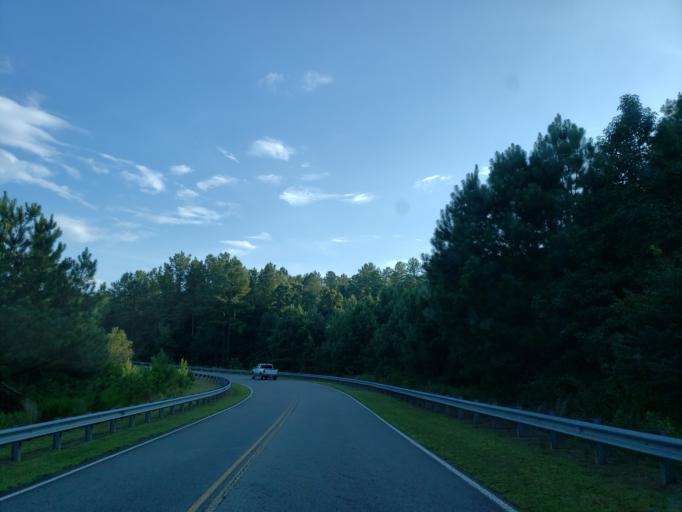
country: US
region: Georgia
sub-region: Cherokee County
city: Canton
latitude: 34.2269
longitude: -84.5736
